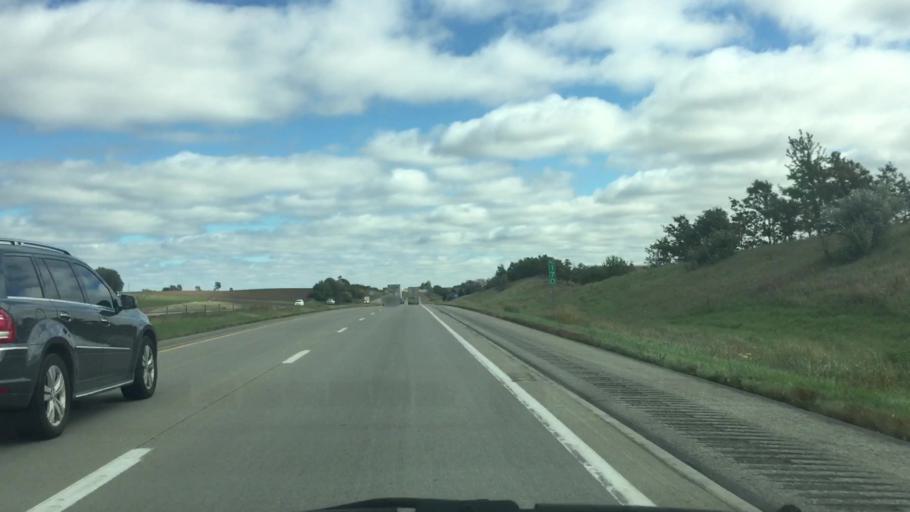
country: US
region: Iowa
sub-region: Jasper County
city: Newton
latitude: 41.6813
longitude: -92.9680
